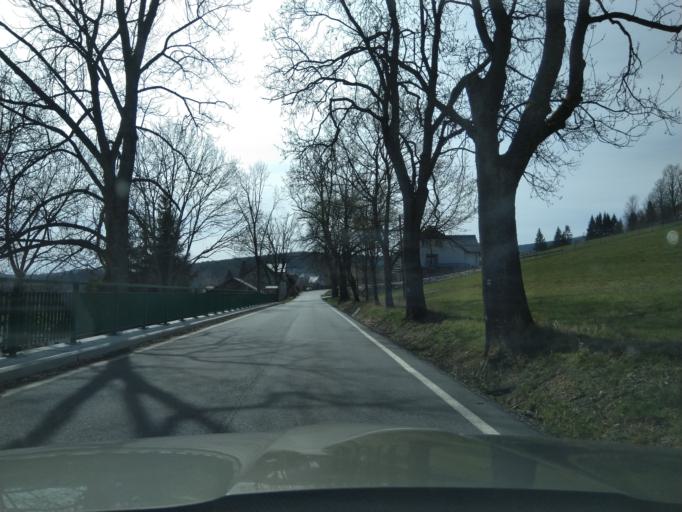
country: CZ
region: Jihocesky
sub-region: Okres Prachatice
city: Stachy
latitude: 49.0876
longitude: 13.6405
